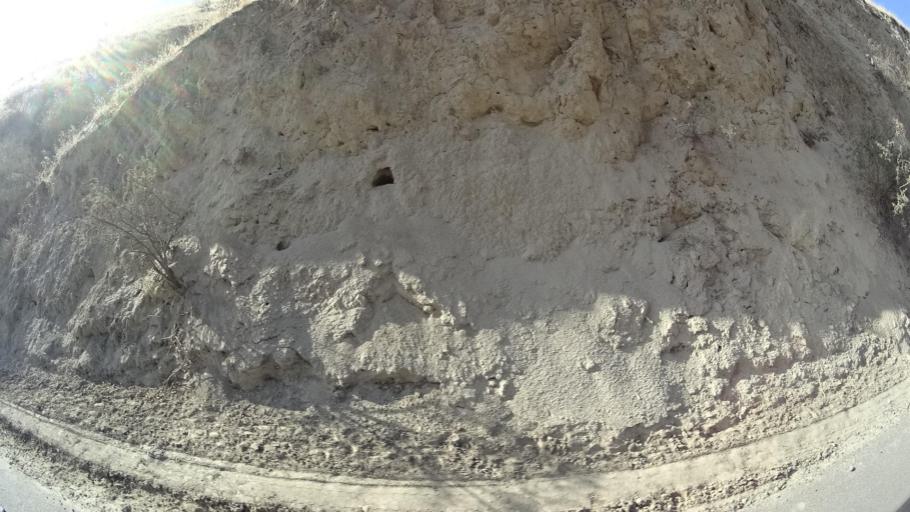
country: US
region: California
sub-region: Kern County
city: Oildale
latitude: 35.5027
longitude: -118.9011
